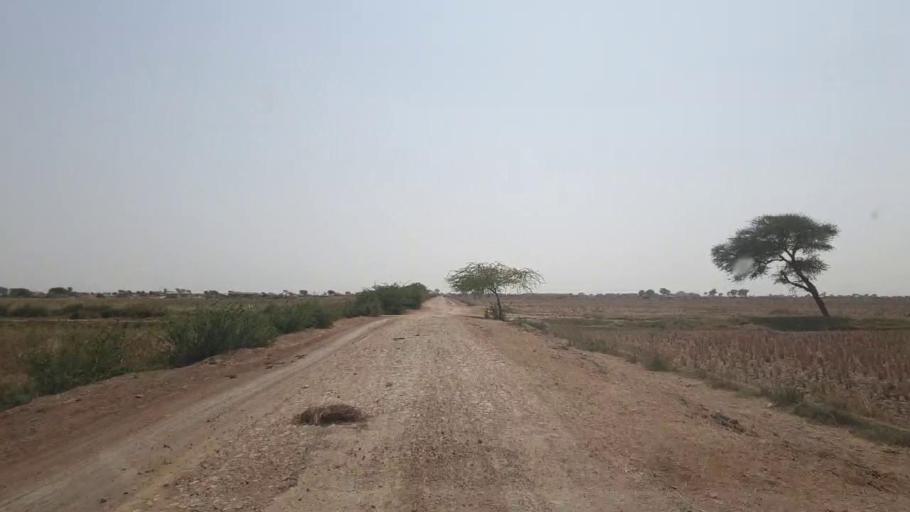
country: PK
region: Sindh
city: Jati
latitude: 24.4314
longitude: 68.5524
